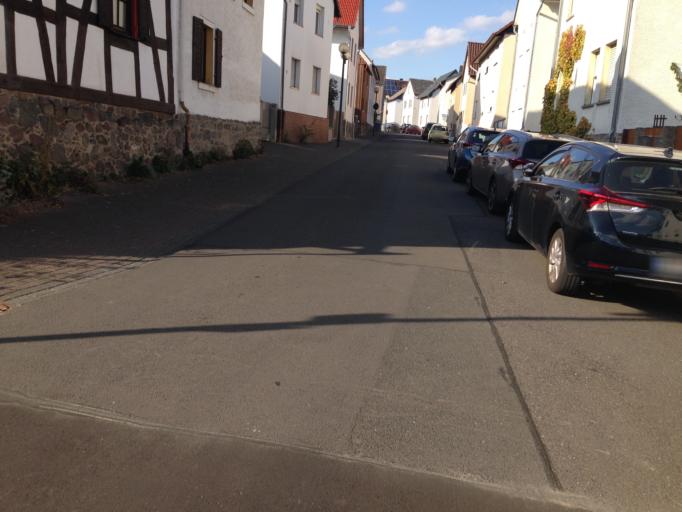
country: DE
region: Hesse
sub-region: Regierungsbezirk Giessen
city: Lich
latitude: 50.5521
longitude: 8.7740
